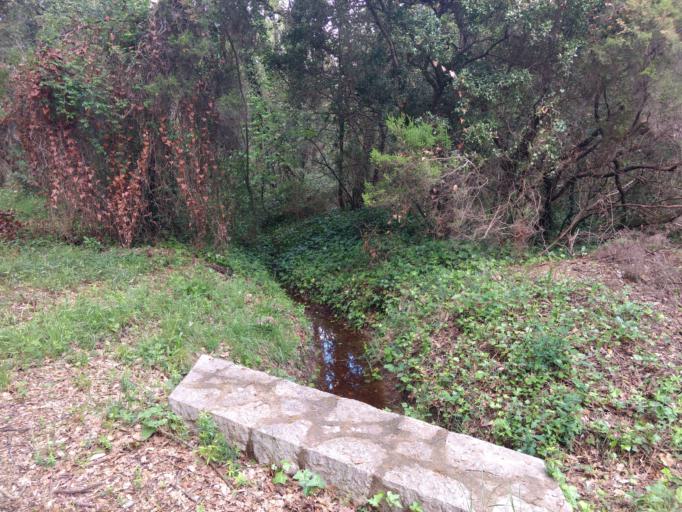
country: FR
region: Provence-Alpes-Cote d'Azur
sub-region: Departement des Alpes-Maritimes
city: Biot
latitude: 43.6221
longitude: 7.1217
